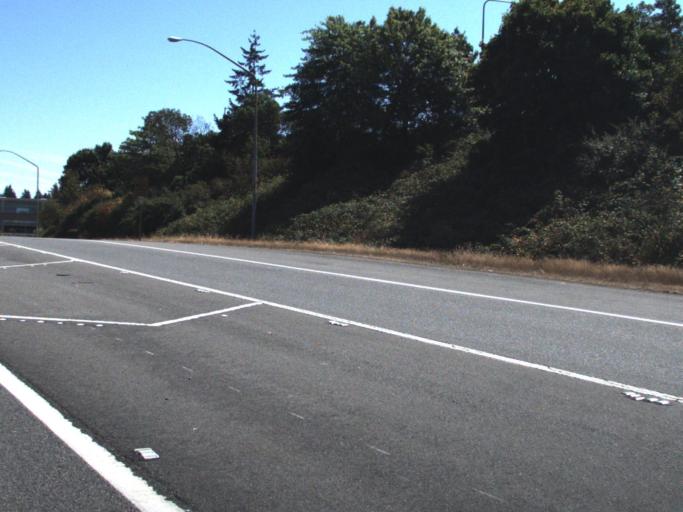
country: US
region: Washington
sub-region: King County
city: SeaTac
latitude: 47.4645
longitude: -122.2984
